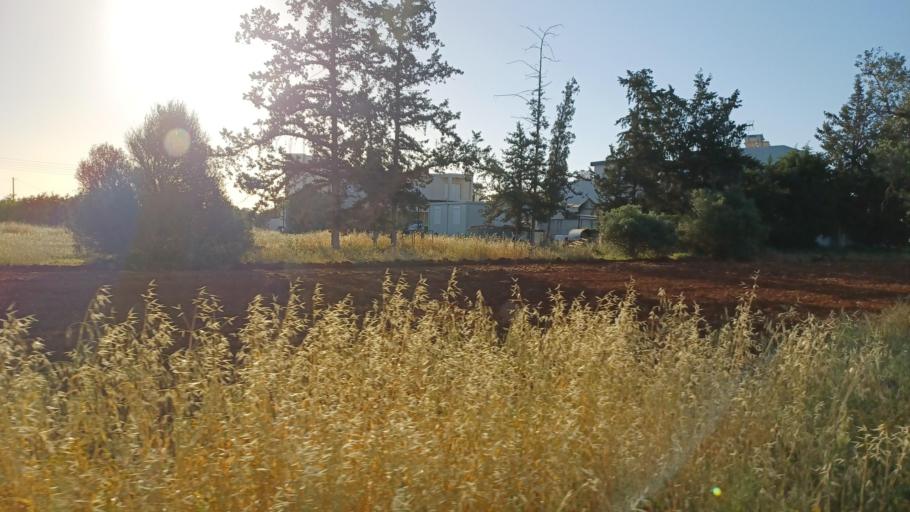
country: CY
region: Lefkosia
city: Kokkinotrimithia
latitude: 35.1469
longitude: 33.1924
